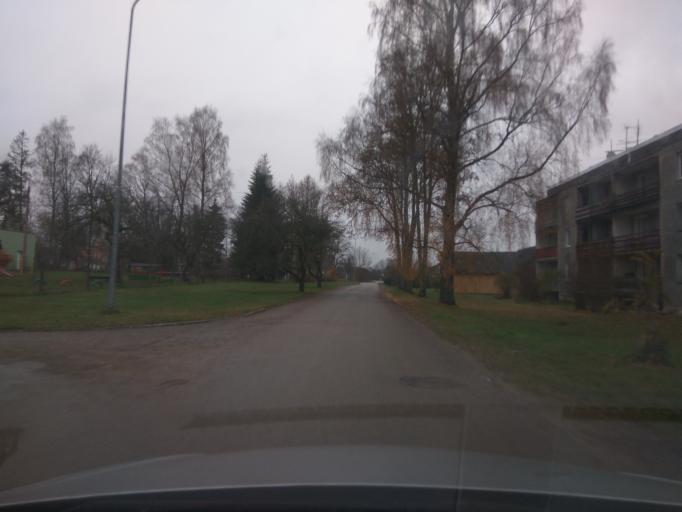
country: LV
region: Kuldigas Rajons
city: Kuldiga
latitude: 56.9206
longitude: 21.9675
